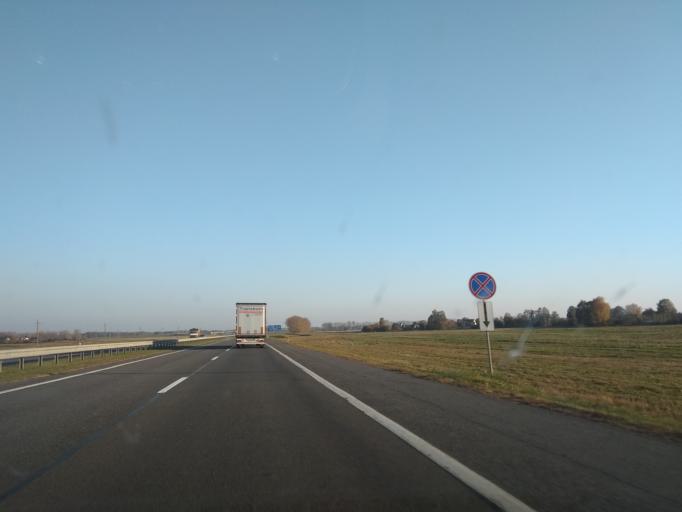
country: BY
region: Brest
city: Kobryn
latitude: 52.1916
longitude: 24.3092
